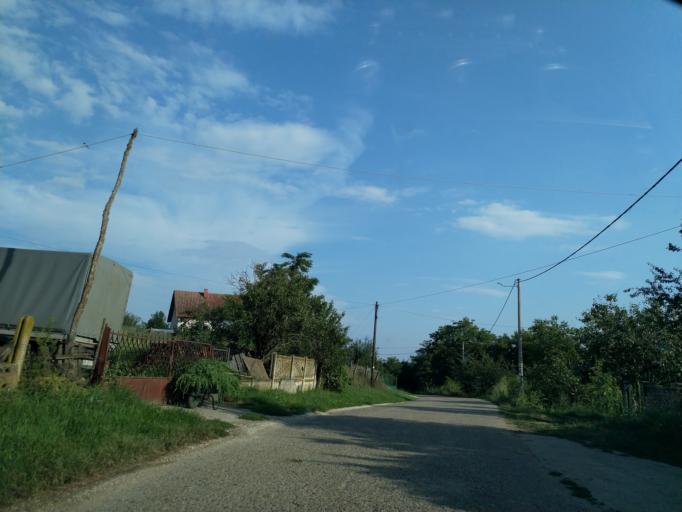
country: RS
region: Central Serbia
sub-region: Pomoravski Okrug
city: Jagodina
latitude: 44.0037
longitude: 21.1838
